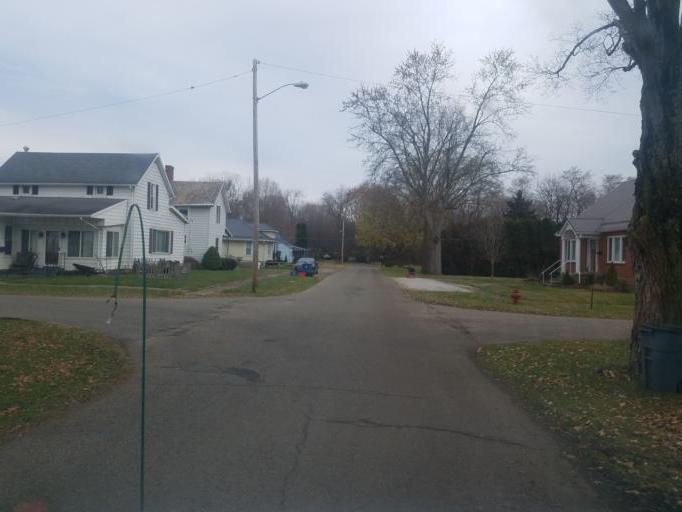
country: US
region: Ohio
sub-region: Knox County
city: Mount Vernon
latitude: 40.3906
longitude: -82.4959
